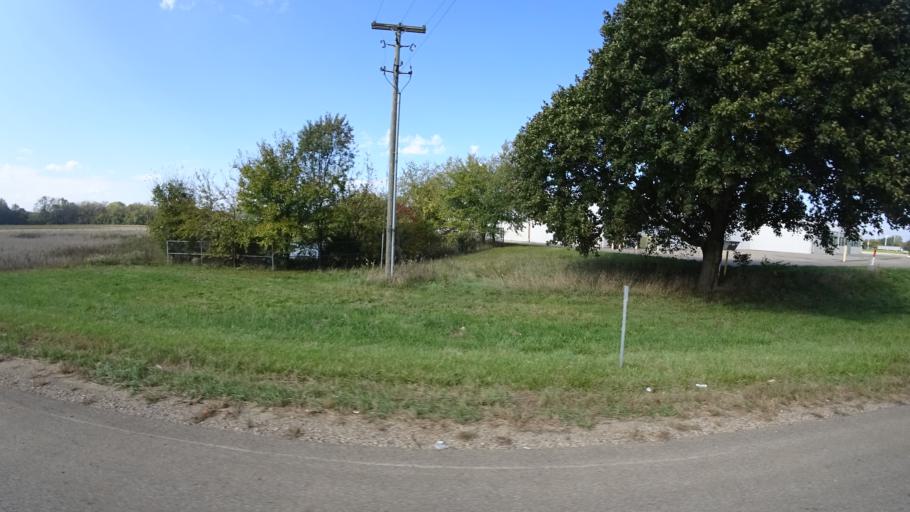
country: US
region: Michigan
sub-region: Saint Joseph County
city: Three Rivers
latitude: 41.9297
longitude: -85.6524
